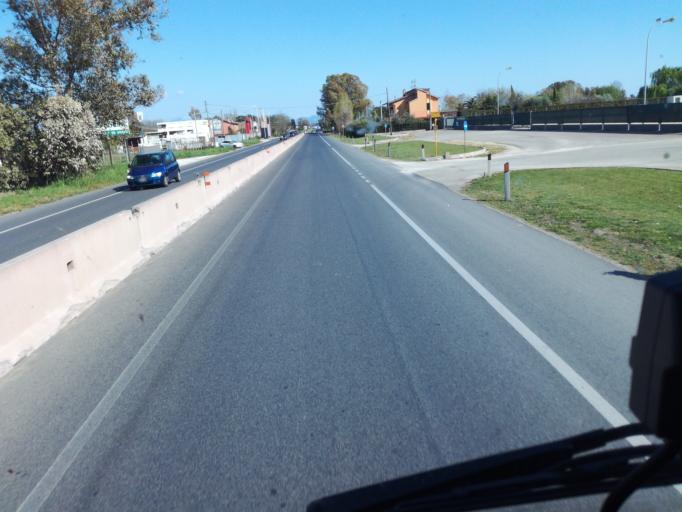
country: IT
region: Latium
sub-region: Provincia di Latina
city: Latina
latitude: 41.4372
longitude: 12.9220
